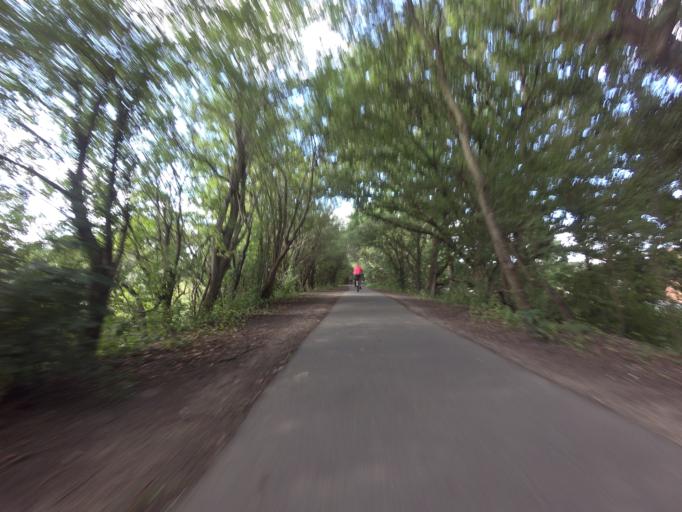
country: GB
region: England
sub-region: East Sussex
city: Hailsham
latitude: 50.8802
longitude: 0.2497
